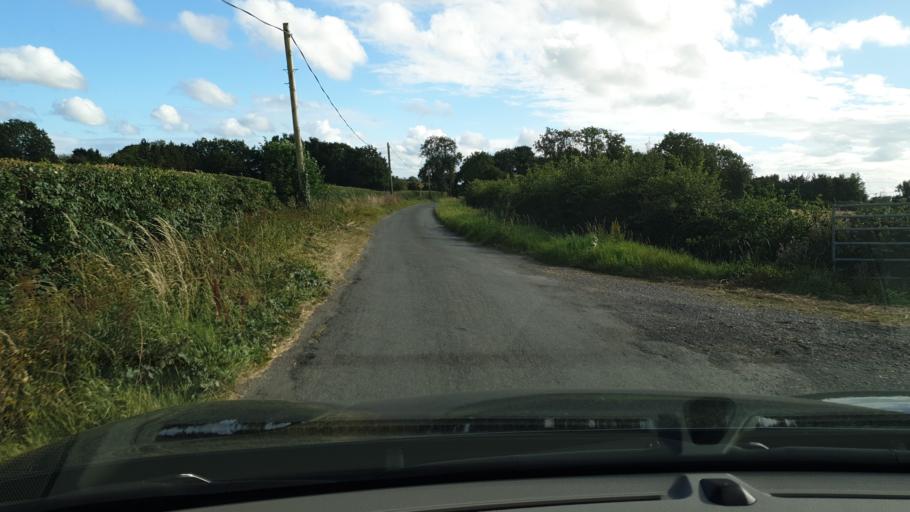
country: IE
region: Leinster
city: Hartstown
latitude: 53.4393
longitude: -6.4307
